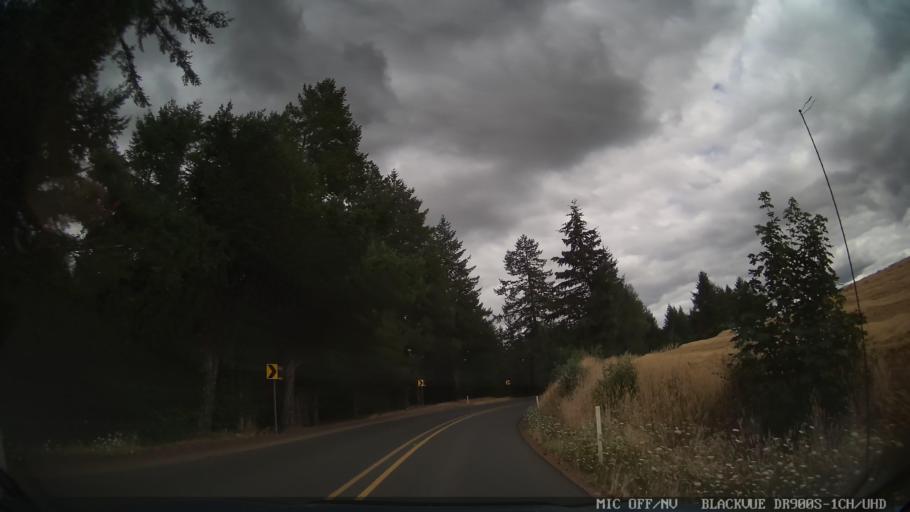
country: US
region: Oregon
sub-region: Linn County
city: Lyons
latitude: 44.8533
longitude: -122.6806
